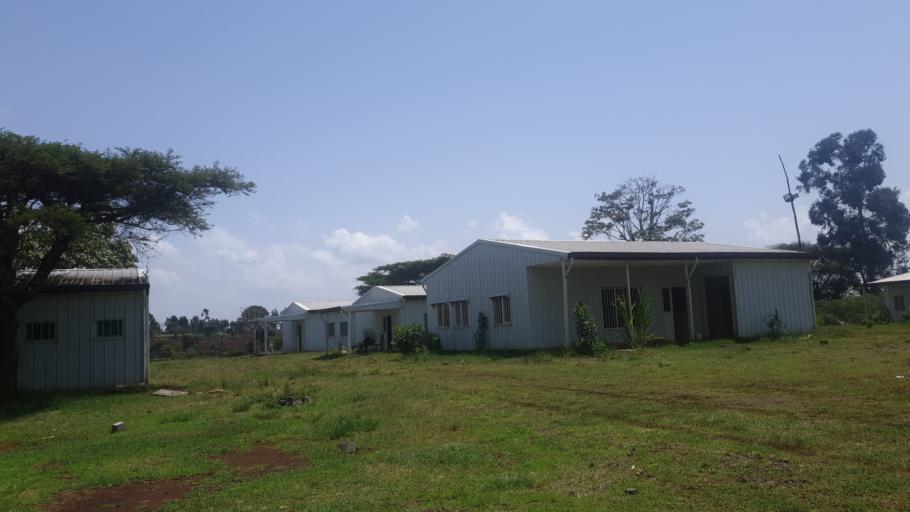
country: ET
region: Oromiya
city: Gedo
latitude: 9.2410
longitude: 37.3546
